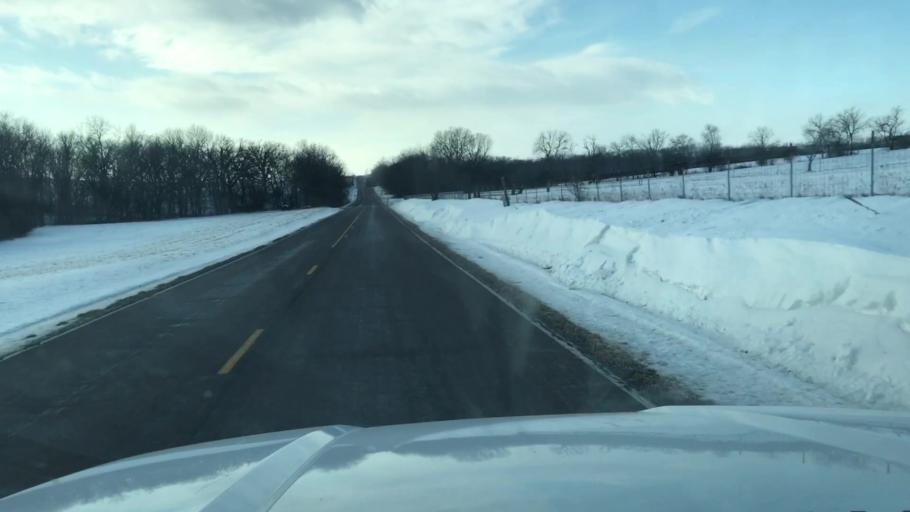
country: US
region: Missouri
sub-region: Nodaway County
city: Maryville
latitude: 40.2018
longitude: -94.9407
